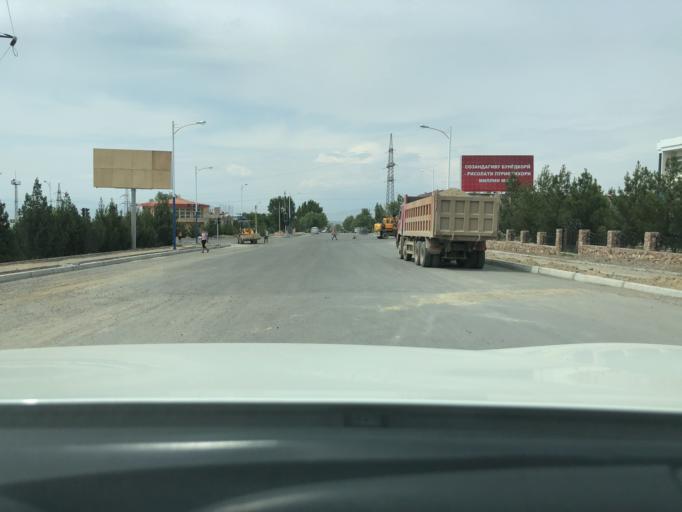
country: TJ
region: Viloyati Sughd
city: Konibodom
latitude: 40.2762
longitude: 70.4445
